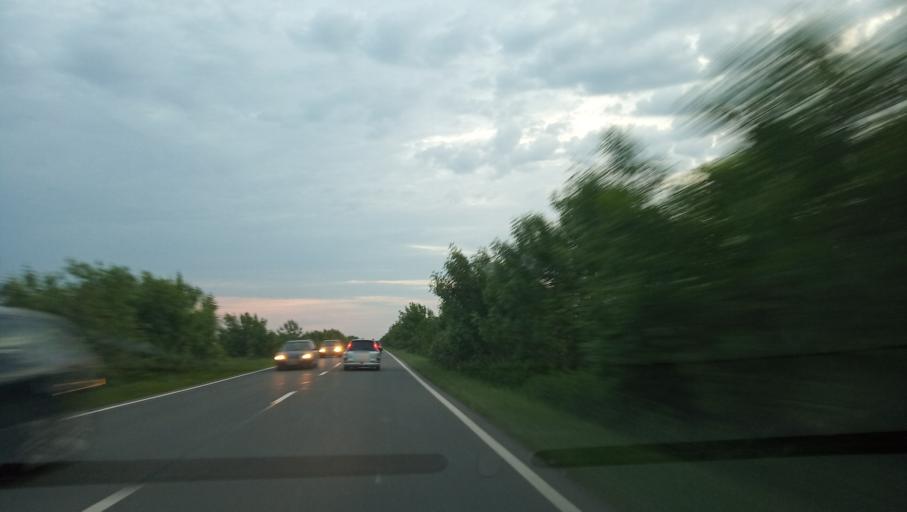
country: RO
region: Timis
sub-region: Comuna Padureni
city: Padureni
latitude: 45.6035
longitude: 21.1971
